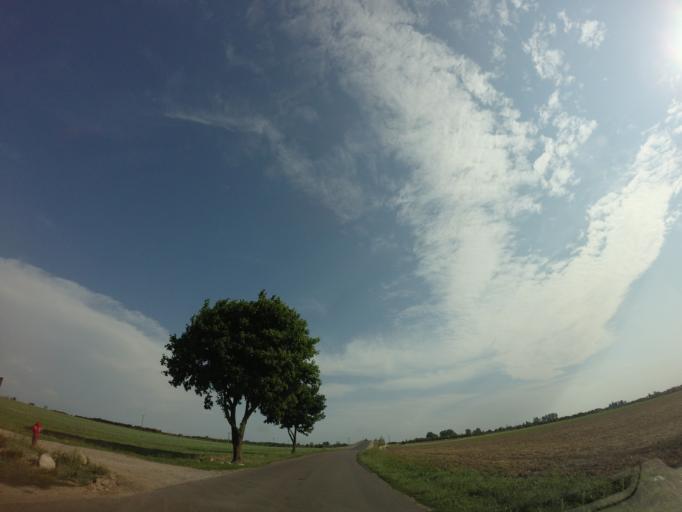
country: PL
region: West Pomeranian Voivodeship
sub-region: Powiat stargardzki
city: Stargard Szczecinski
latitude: 53.3093
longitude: 15.0458
